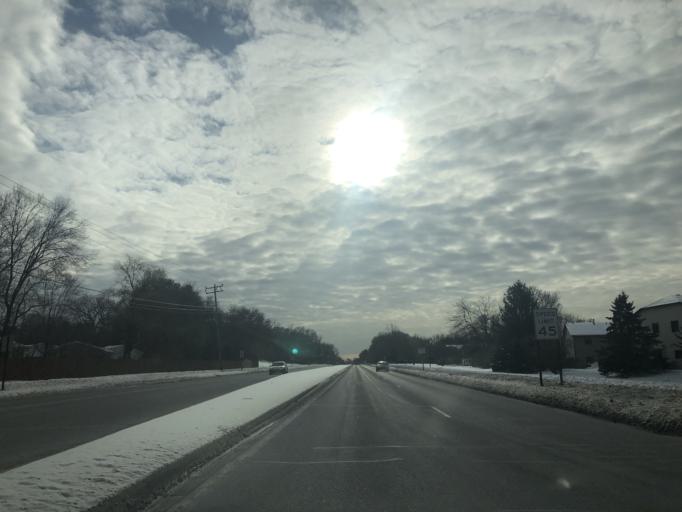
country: US
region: Minnesota
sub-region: Anoka County
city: Lexington
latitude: 45.1523
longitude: -93.1635
